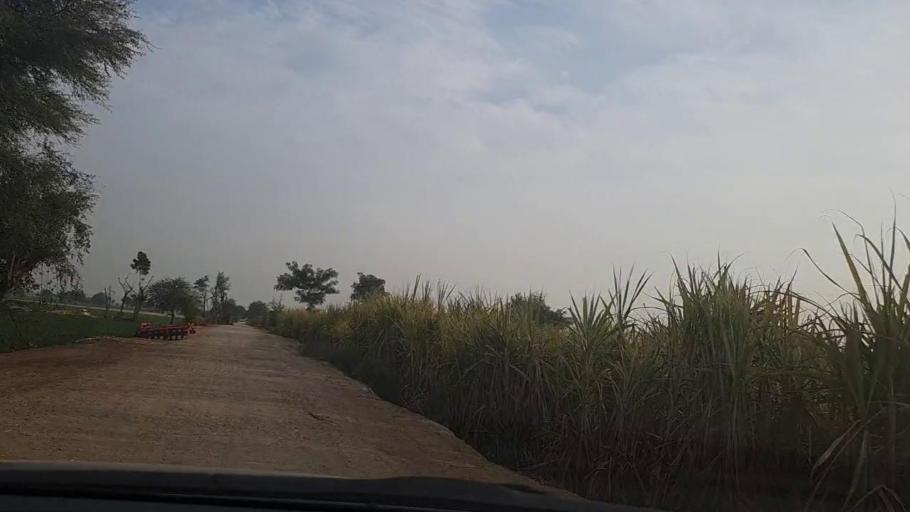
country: PK
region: Sindh
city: Daulatpur
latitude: 26.3303
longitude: 68.0247
